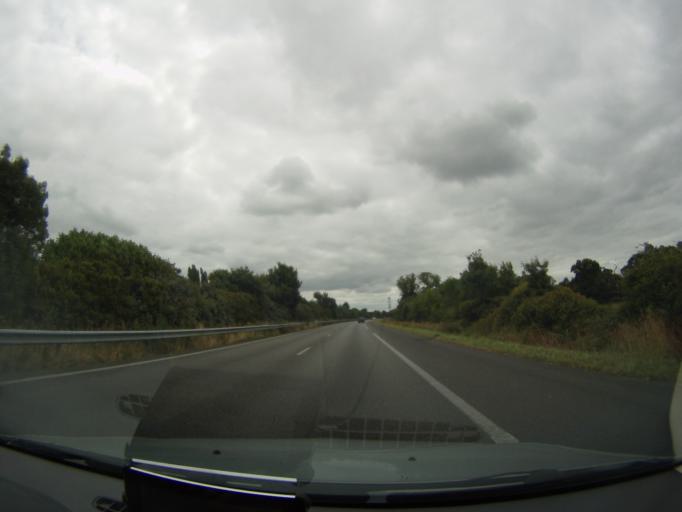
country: FR
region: Pays de la Loire
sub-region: Departement de la Loire-Atlantique
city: Heric
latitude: 47.4312
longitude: -1.6383
